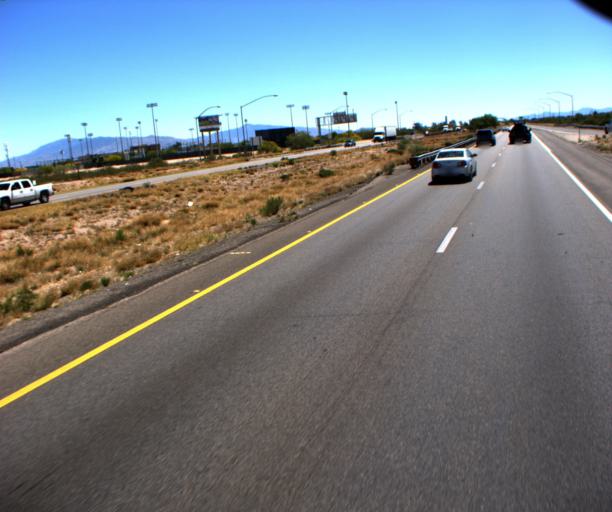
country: US
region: Arizona
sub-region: Pima County
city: South Tucson
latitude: 32.1758
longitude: -110.9422
